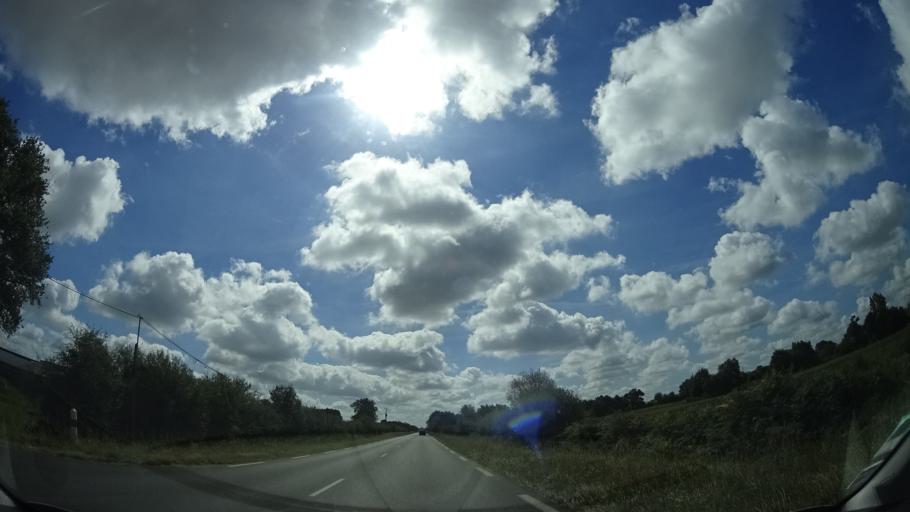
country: FR
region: Pays de la Loire
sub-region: Departement de la Mayenne
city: Meslay-du-Maine
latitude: 47.9788
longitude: -0.6061
